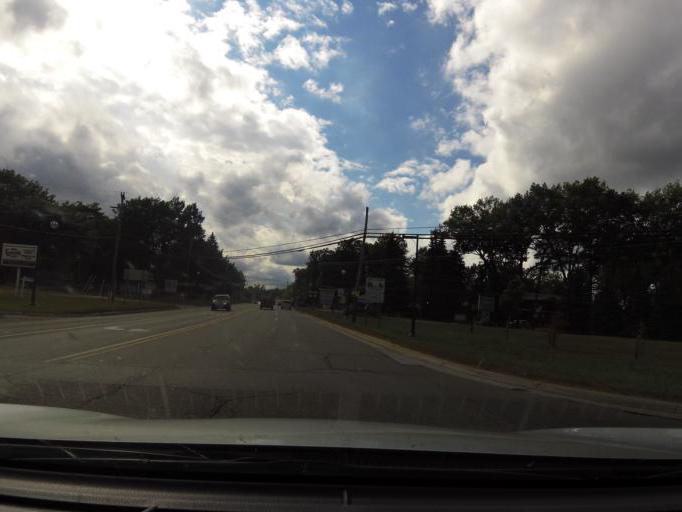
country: US
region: Michigan
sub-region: Roscommon County
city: Prudenville
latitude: 44.3054
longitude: -84.6396
